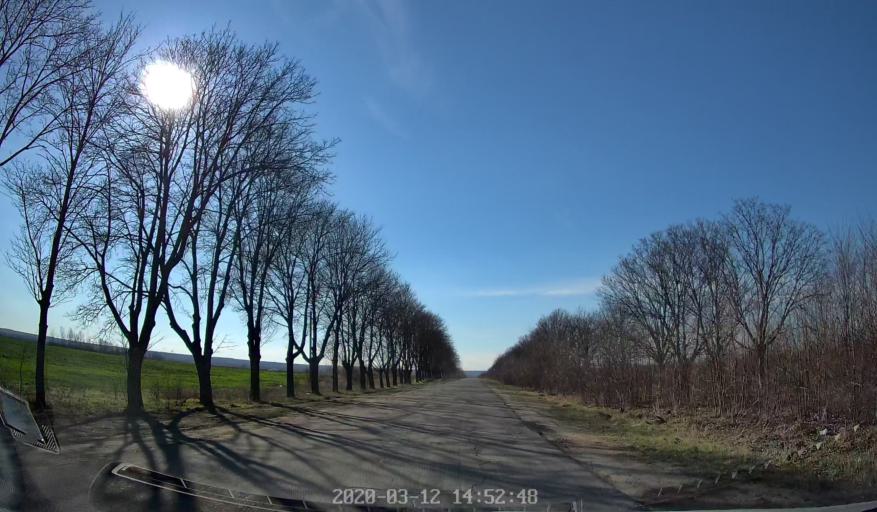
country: MD
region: Criuleni
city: Criuleni
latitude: 47.2194
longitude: 29.0919
